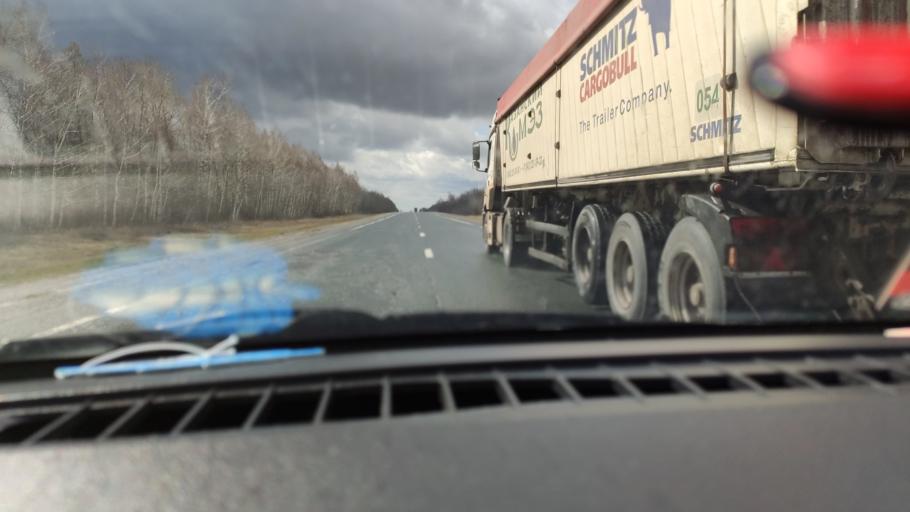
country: RU
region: Samara
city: Yelkhovka
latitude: 53.9474
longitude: 50.2663
